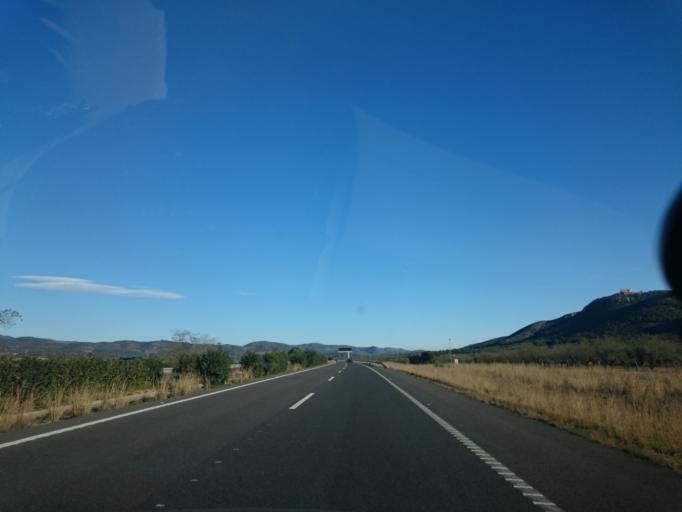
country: ES
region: Valencia
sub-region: Provincia de Castello
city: Alcala de Xivert
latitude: 40.2975
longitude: 0.2342
